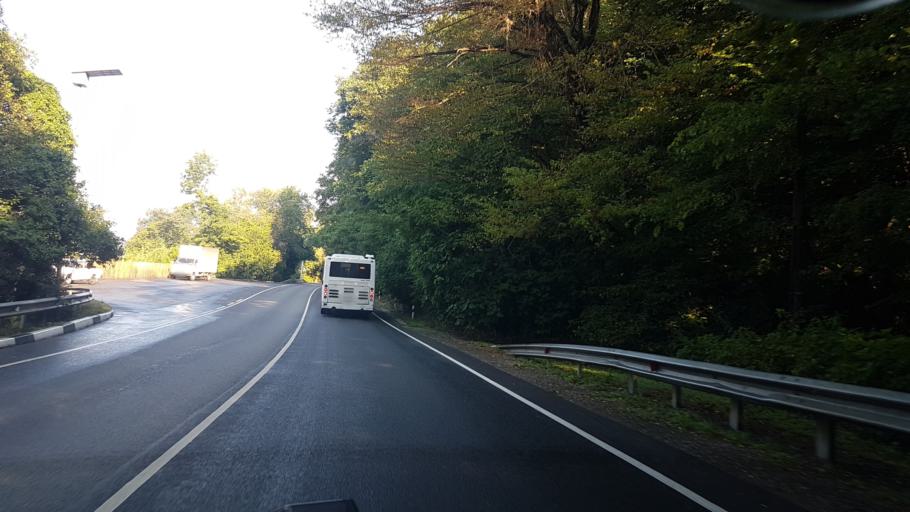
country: RU
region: Krasnodarskiy
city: Vardane
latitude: 43.7753
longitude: 39.4857
